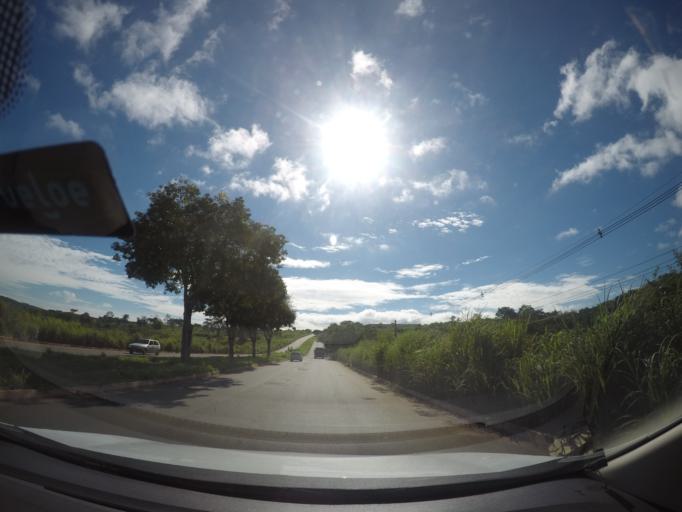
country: BR
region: Goias
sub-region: Goiania
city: Goiania
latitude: -16.6512
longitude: -49.1673
